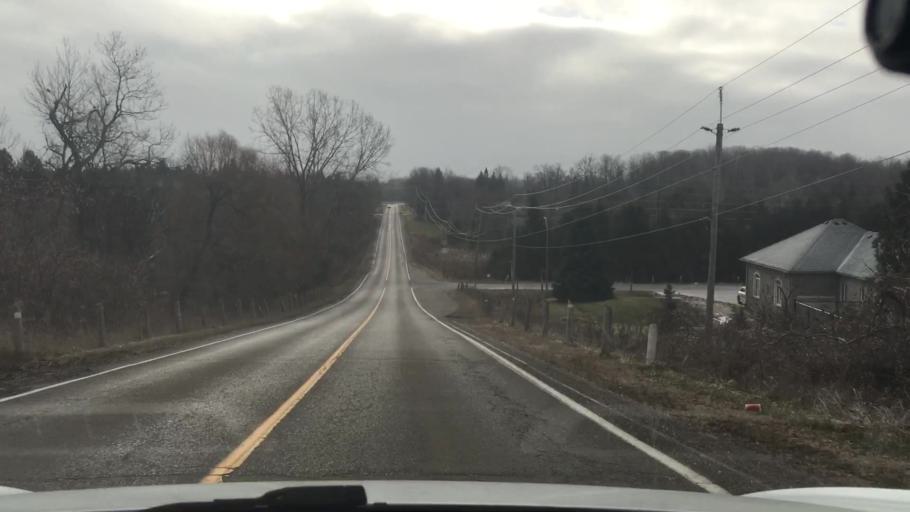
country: CA
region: Ontario
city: Oshawa
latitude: 43.9368
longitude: -78.7999
